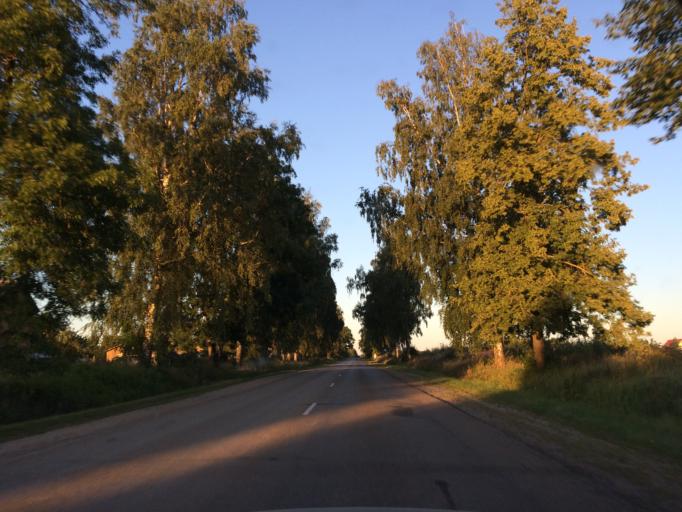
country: LV
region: Rezekne
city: Rezekne
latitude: 56.5140
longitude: 27.3830
